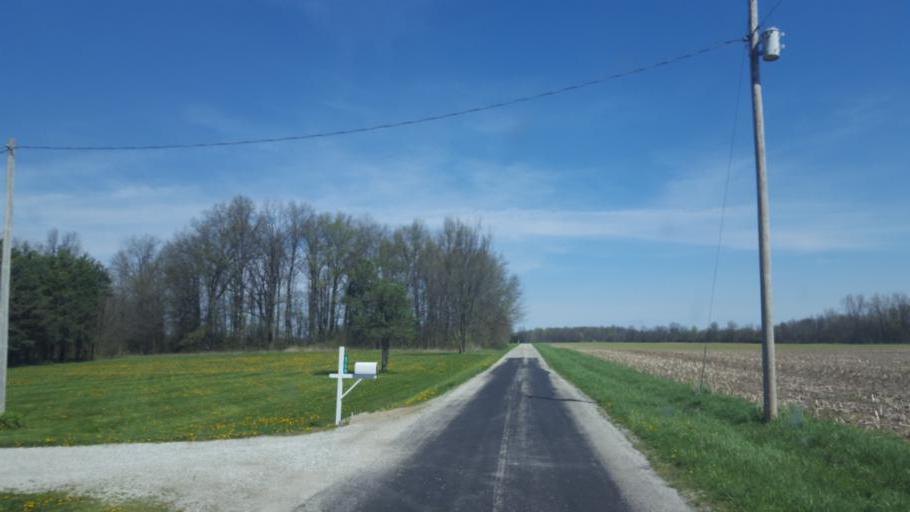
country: US
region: Ohio
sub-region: Morrow County
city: Mount Gilead
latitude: 40.6073
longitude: -82.8853
